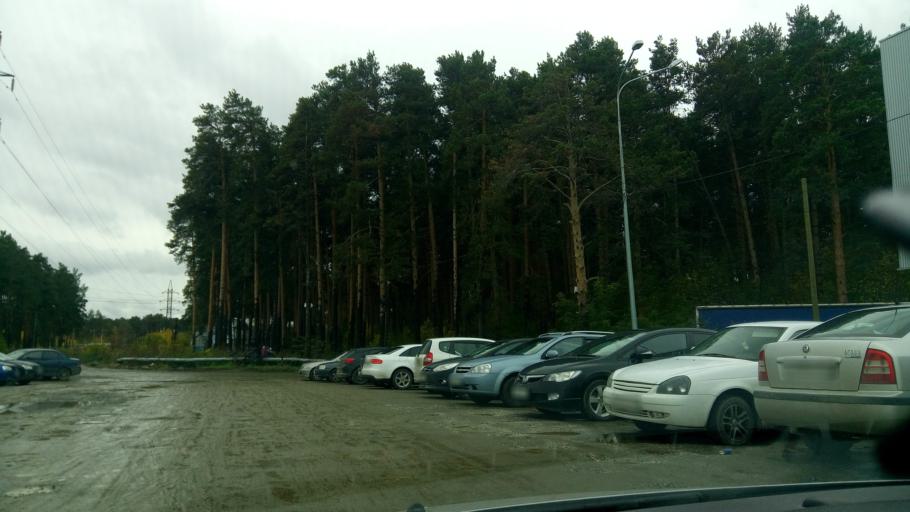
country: RU
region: Sverdlovsk
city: Shirokaya Rechka
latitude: 56.8194
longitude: 60.5228
